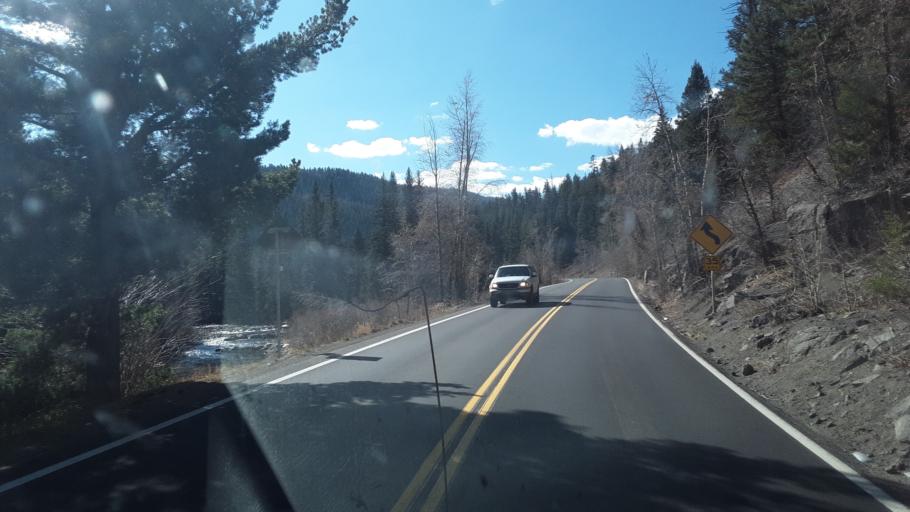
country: US
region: Colorado
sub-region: Mineral County
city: Creede
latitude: 37.5951
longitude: -106.7288
